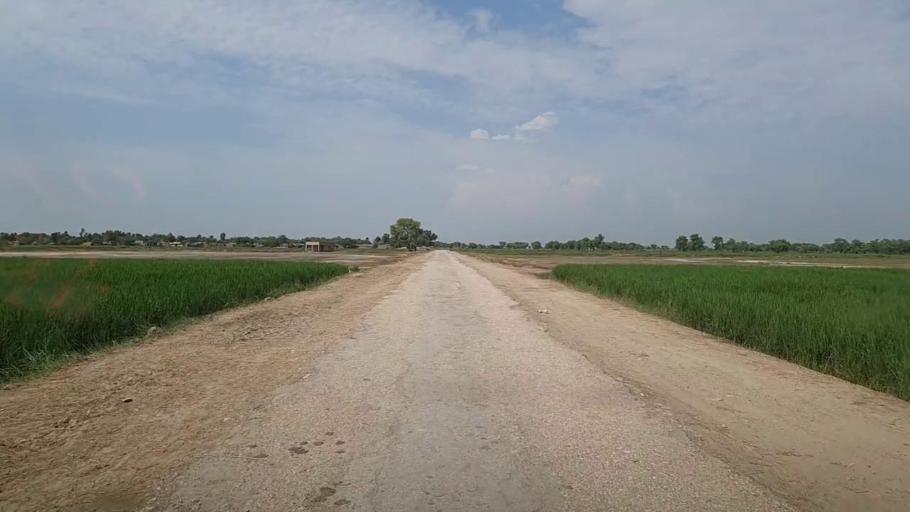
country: PK
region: Sindh
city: Thul
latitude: 28.2404
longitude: 68.8102
